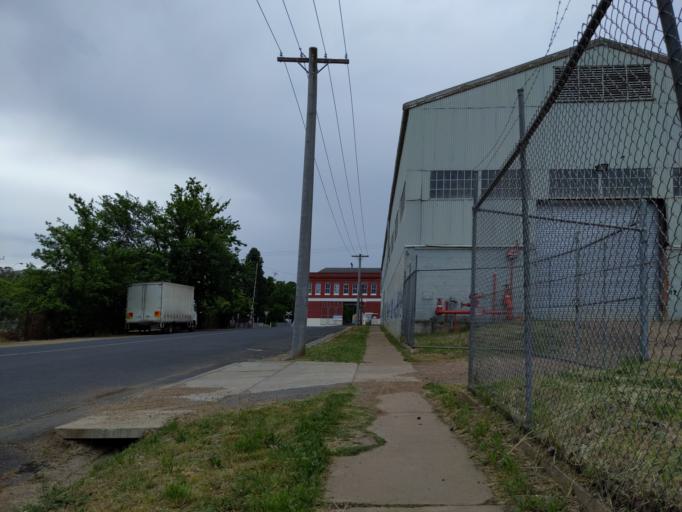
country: AU
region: Victoria
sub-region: Mount Alexander
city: Castlemaine
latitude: -37.0568
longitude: 144.2158
